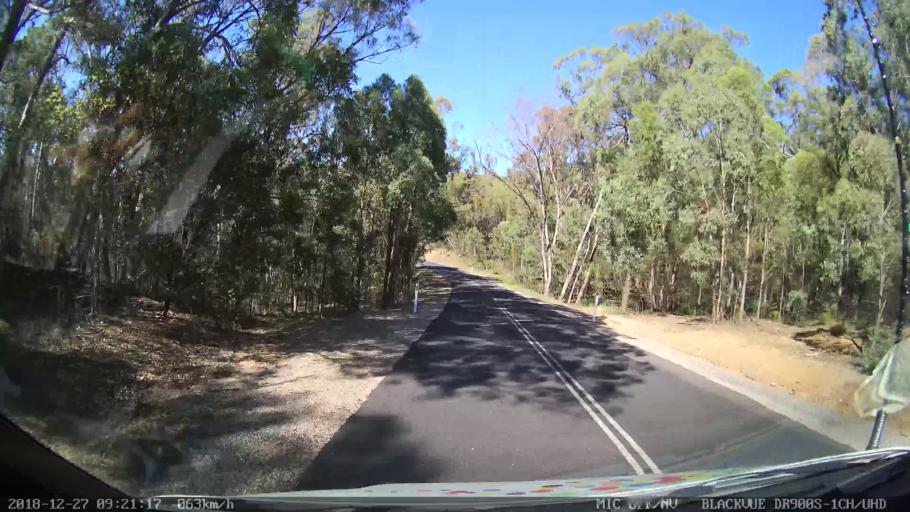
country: AU
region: New South Wales
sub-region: Lithgow
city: Portland
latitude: -33.1226
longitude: 150.0174
